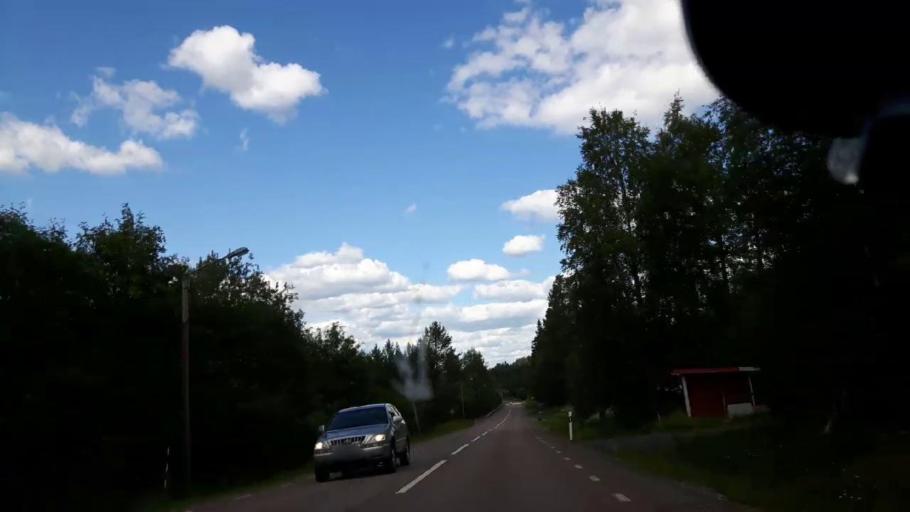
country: SE
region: Jaemtland
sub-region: Ragunda Kommun
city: Hammarstrand
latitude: 62.9935
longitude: 16.6770
